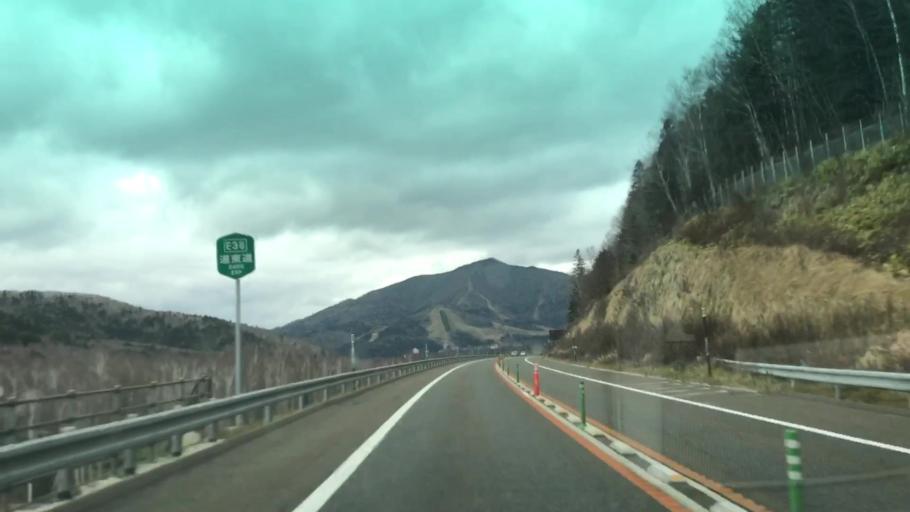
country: JP
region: Hokkaido
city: Shimo-furano
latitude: 43.0458
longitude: 142.6554
